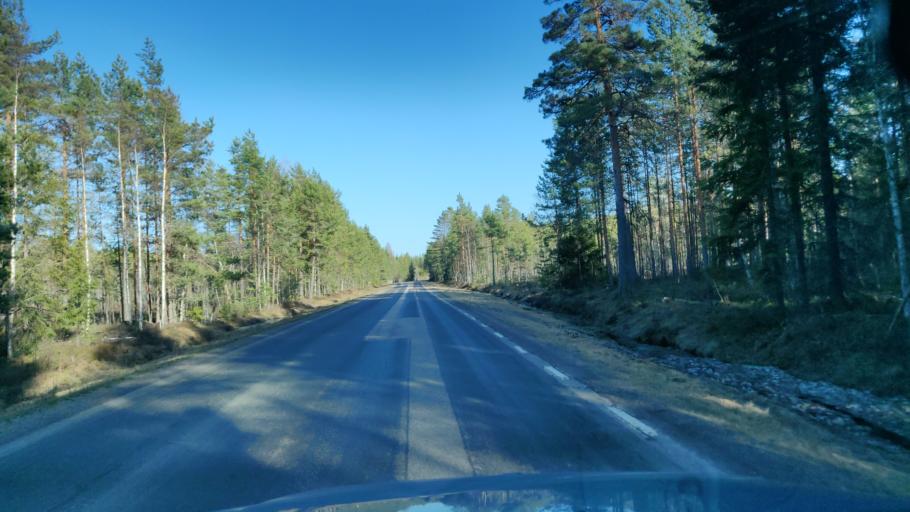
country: SE
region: Vaermland
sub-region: Sunne Kommun
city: Sunne
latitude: 59.9865
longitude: 13.3365
